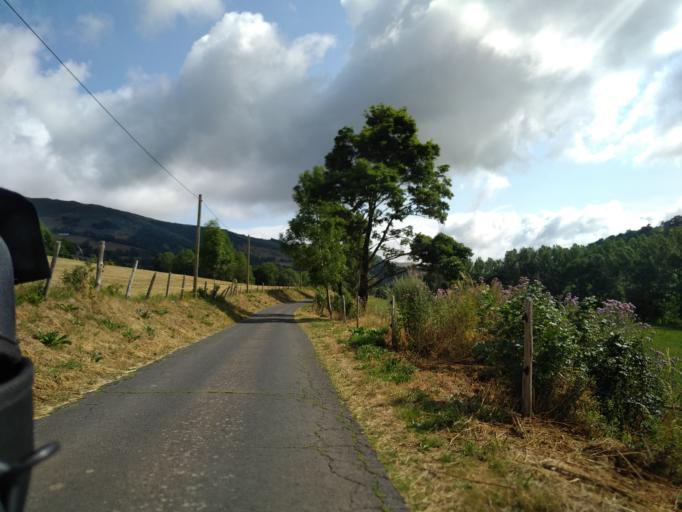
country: FR
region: Auvergne
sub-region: Departement du Cantal
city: Murat
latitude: 45.1265
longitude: 2.7396
